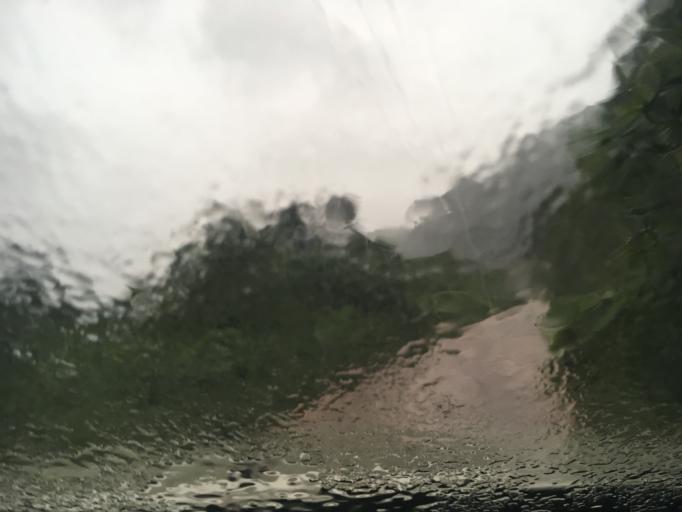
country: LA
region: Oudomxai
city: Muang La
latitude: 21.2275
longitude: 101.9609
